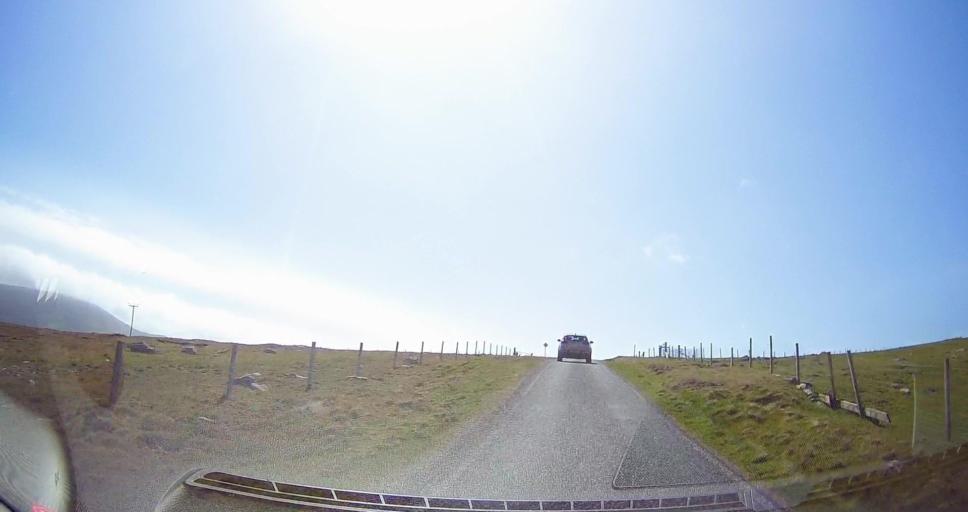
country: GB
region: Scotland
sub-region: Shetland Islands
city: Sandwick
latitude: 60.0782
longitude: -1.3382
